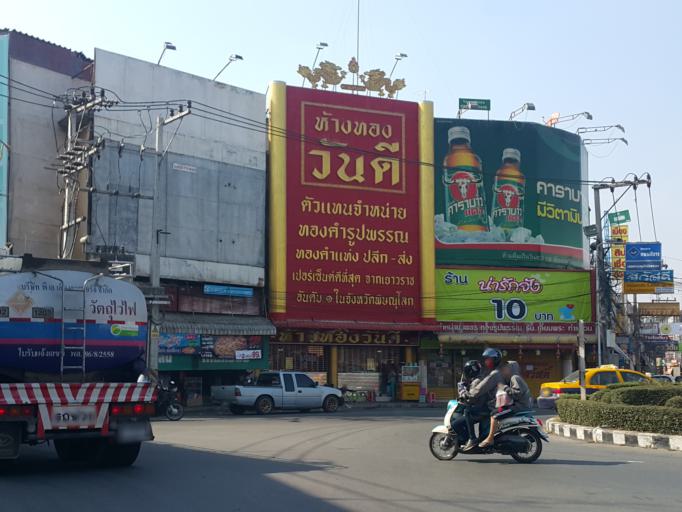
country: TH
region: Phitsanulok
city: Phitsanulok
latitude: 16.8147
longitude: 100.2647
